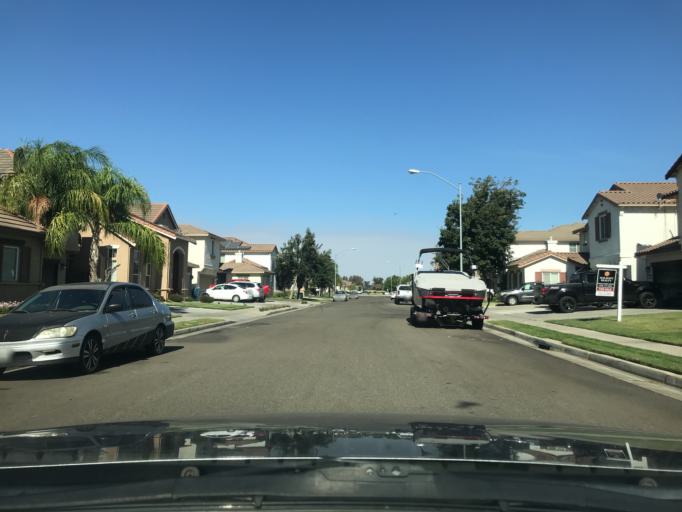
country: US
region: California
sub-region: Merced County
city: Atwater
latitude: 37.3411
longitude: -120.5763
